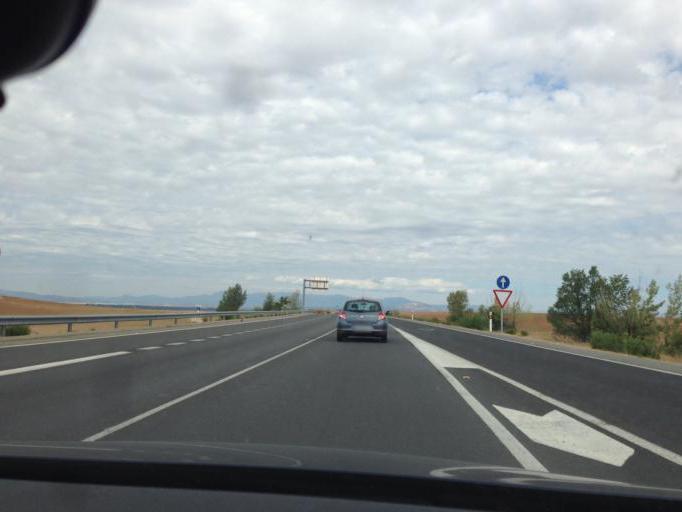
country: ES
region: Madrid
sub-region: Provincia de Madrid
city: Cobena
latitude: 40.5697
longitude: -3.5209
